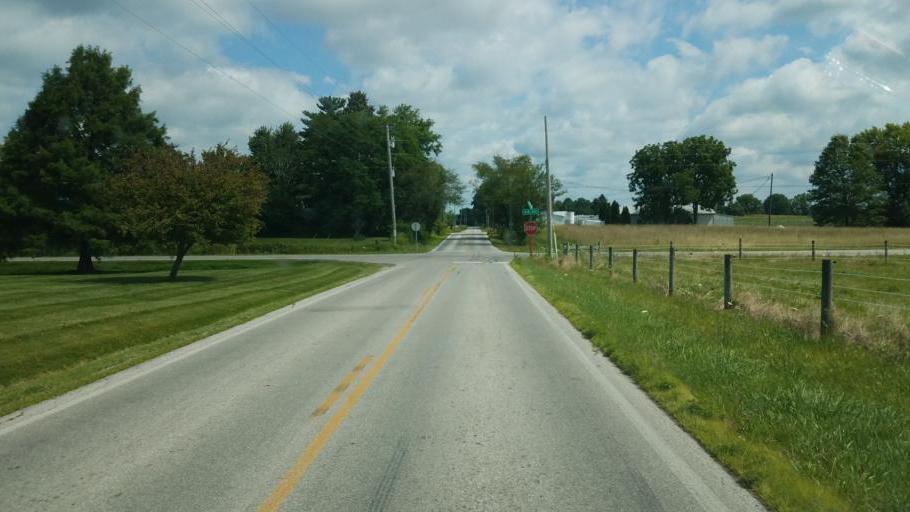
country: US
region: Ohio
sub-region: Delaware County
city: Ashley
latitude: 40.3270
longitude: -82.9321
